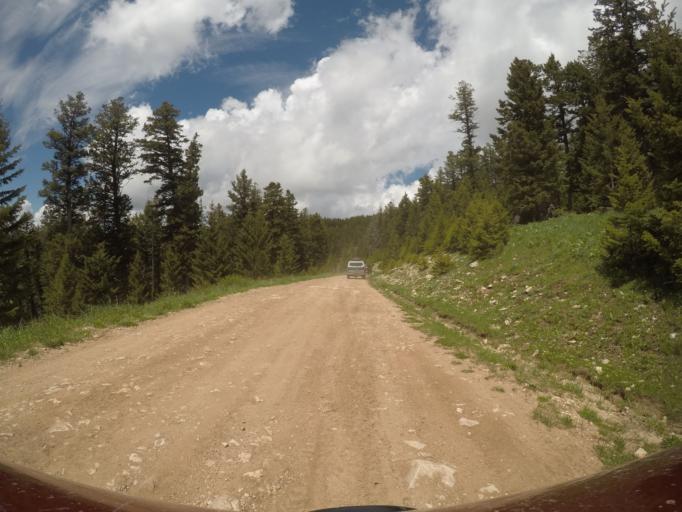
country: US
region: Wyoming
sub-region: Big Horn County
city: Lovell
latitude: 45.1655
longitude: -108.4084
